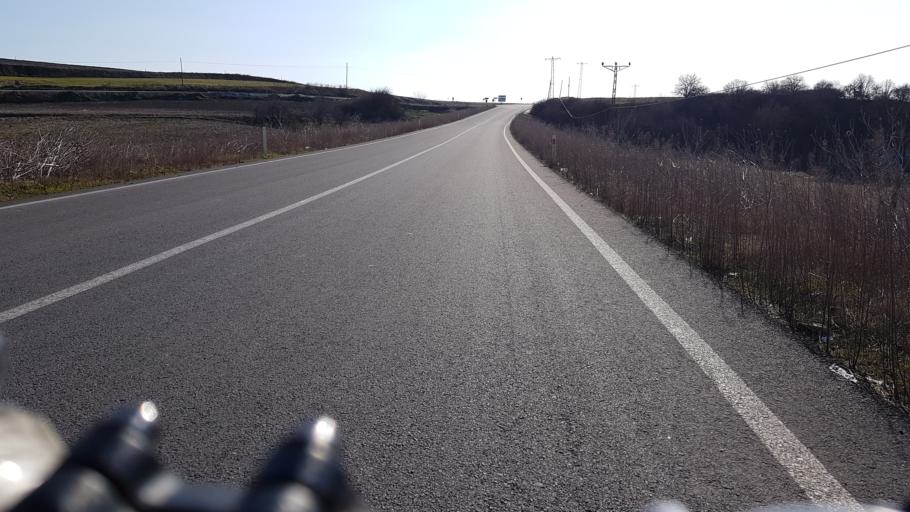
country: TR
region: Tekirdag
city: Velimese
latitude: 41.3566
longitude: 27.8500
